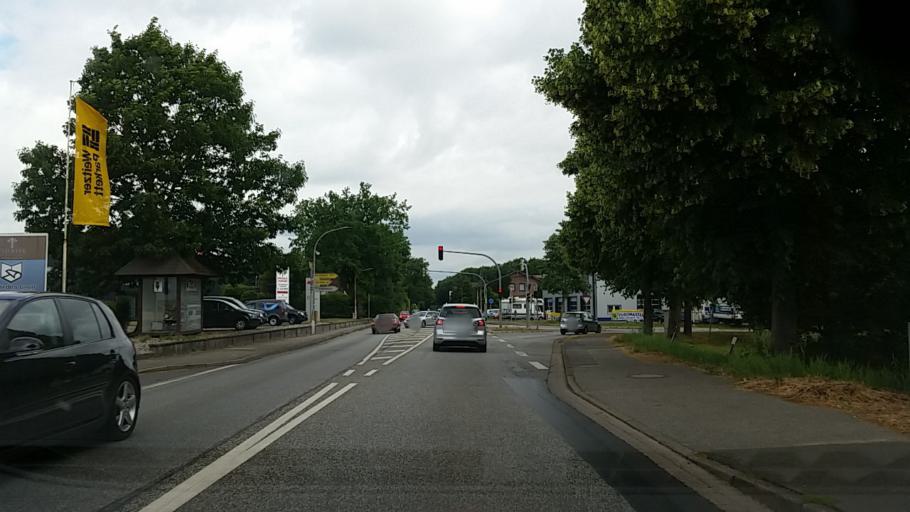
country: DE
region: Schleswig-Holstein
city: Kayhude
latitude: 53.7506
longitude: 10.1268
